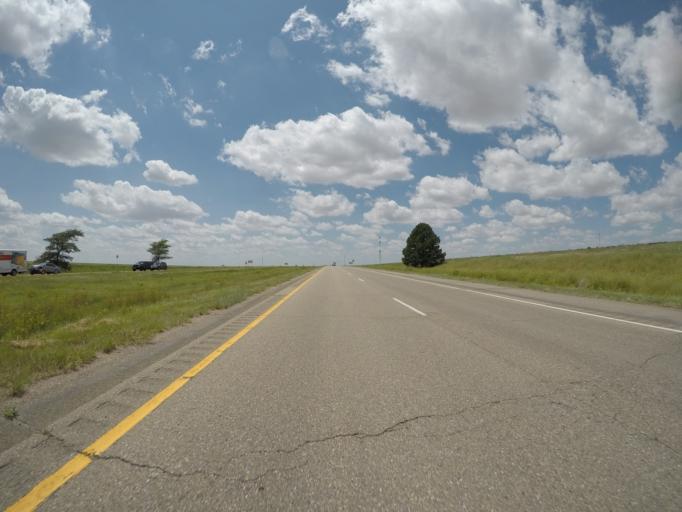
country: US
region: Colorado
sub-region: Kit Carson County
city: Burlington
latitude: 39.2941
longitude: -102.4289
